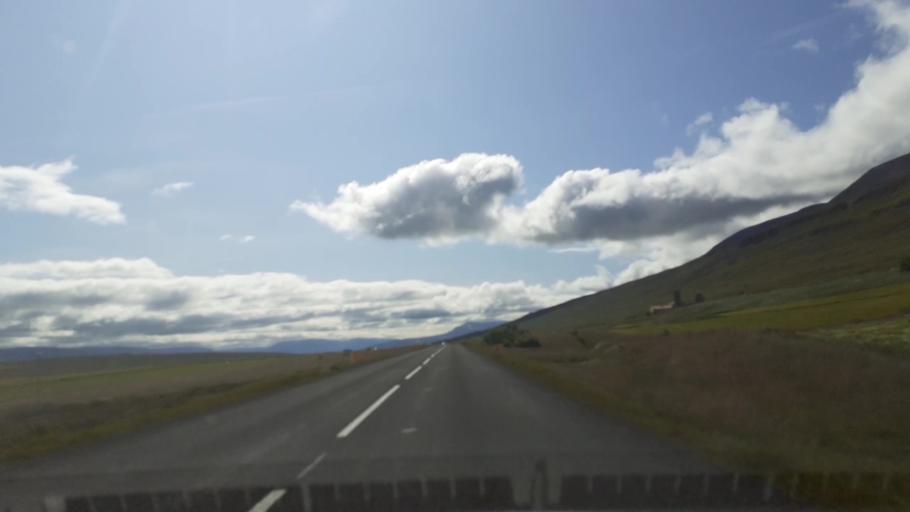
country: IS
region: Northeast
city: Akureyri
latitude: 65.8618
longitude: -18.2606
